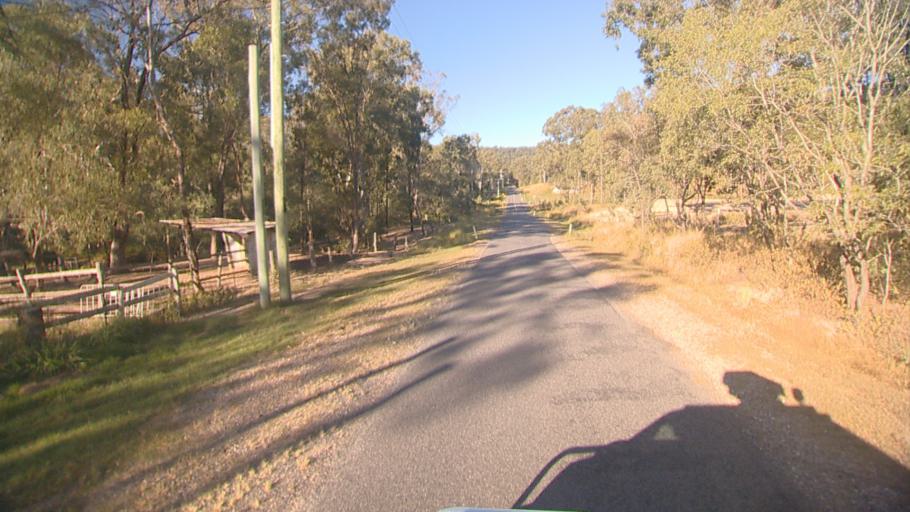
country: AU
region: Queensland
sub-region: Logan
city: Windaroo
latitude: -27.7714
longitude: 153.1441
